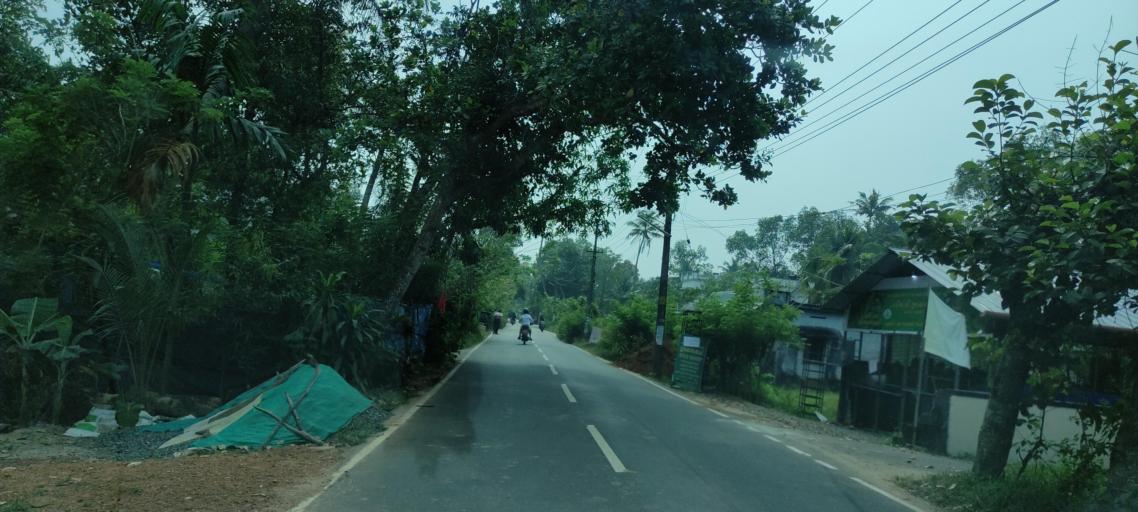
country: IN
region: Kerala
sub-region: Alappuzha
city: Alleppey
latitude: 9.5492
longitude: 76.3330
